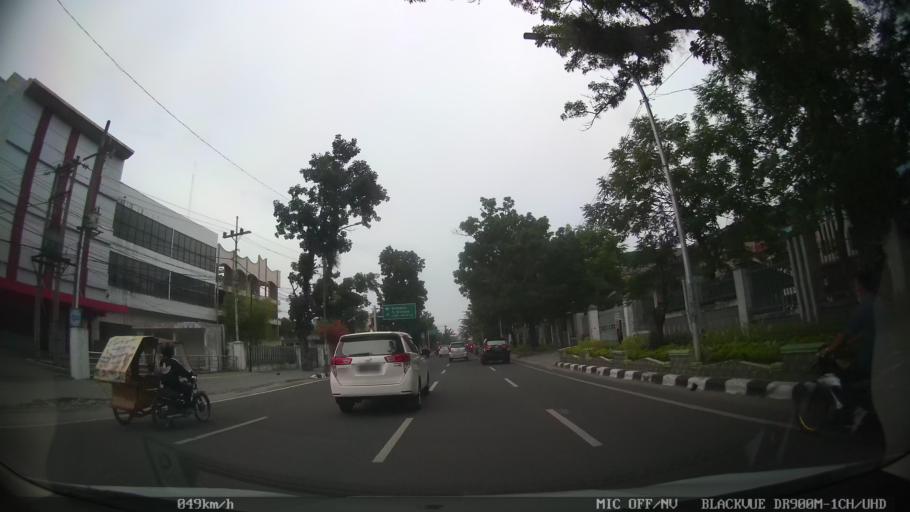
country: ID
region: North Sumatra
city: Medan
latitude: 3.5975
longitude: 98.6802
